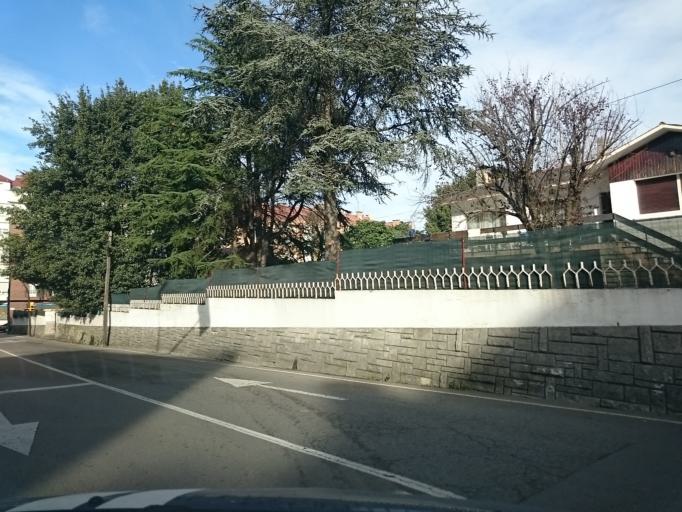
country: ES
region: Asturias
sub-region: Province of Asturias
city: Gijon
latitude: 43.5196
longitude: -5.6634
